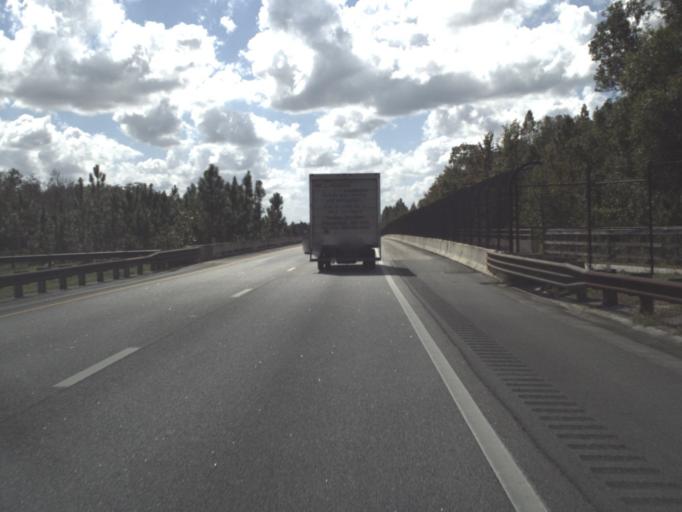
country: US
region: Florida
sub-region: Pasco County
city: Odessa
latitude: 28.2392
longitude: -82.5507
